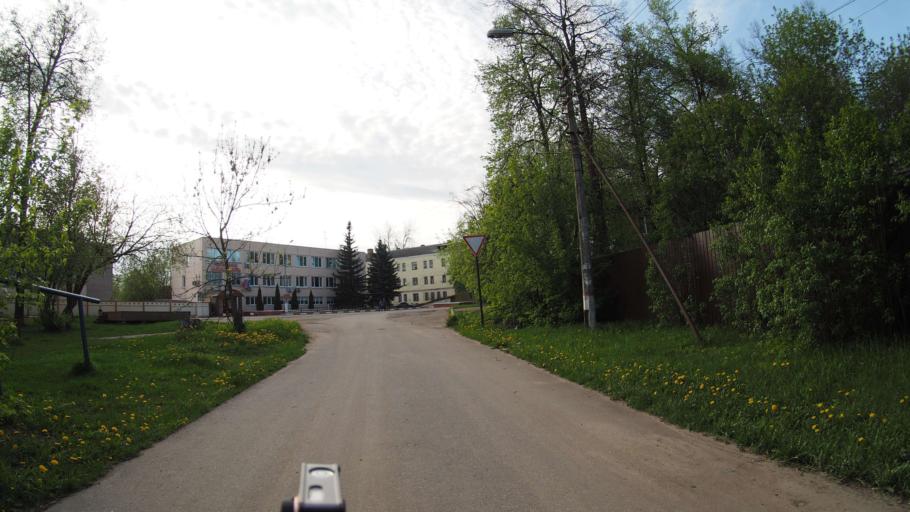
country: RU
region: Moskovskaya
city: Ramenskoye
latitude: 55.5682
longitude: 38.2090
